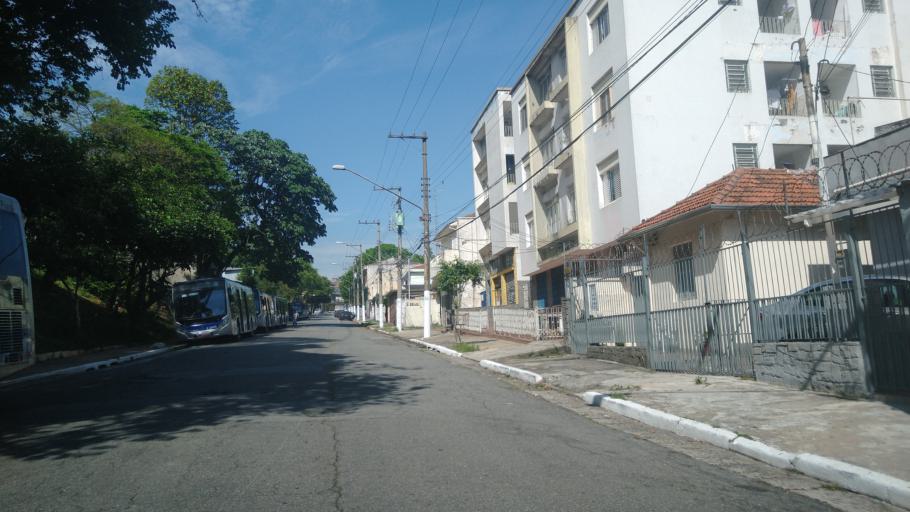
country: BR
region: Sao Paulo
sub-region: Sao Paulo
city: Sao Paulo
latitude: -23.4929
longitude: -46.6740
